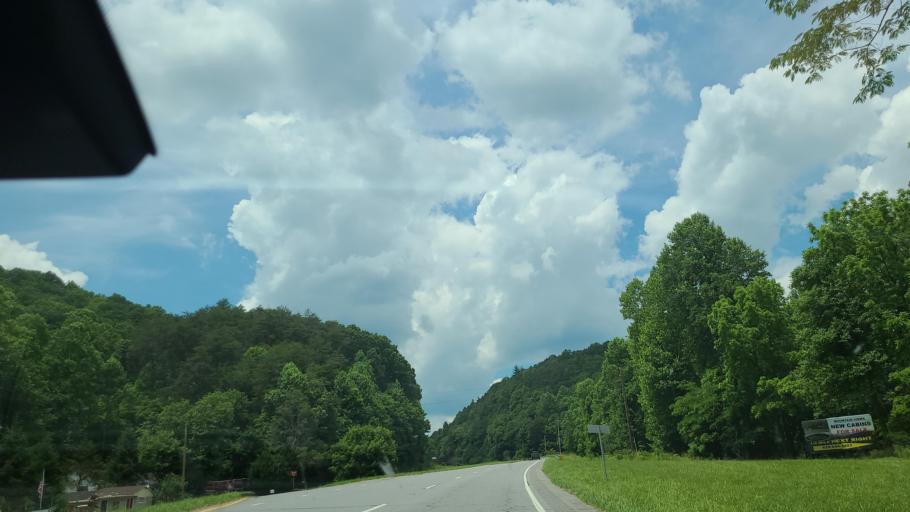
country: US
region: Georgia
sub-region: Fannin County
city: McCaysville
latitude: 35.0166
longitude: -84.3128
